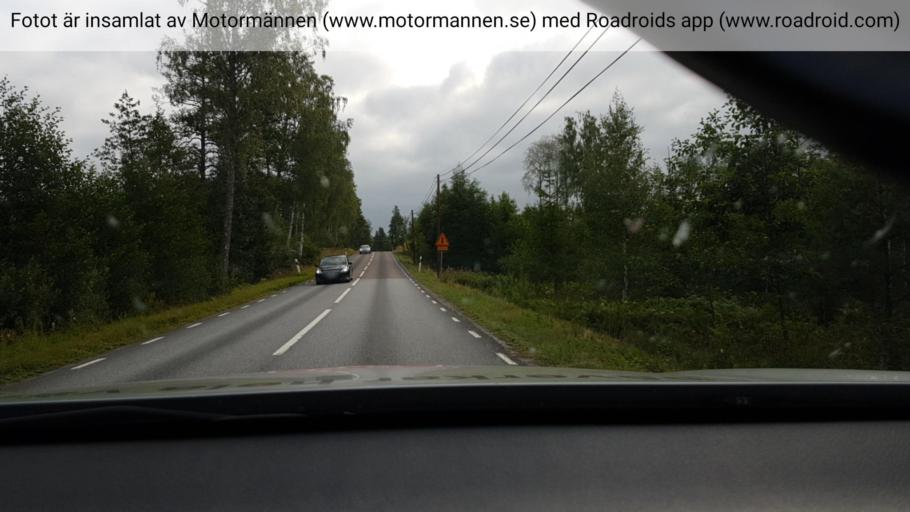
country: SE
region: Stockholm
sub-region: Norrtalje Kommun
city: Rimbo
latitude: 59.7704
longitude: 18.4262
